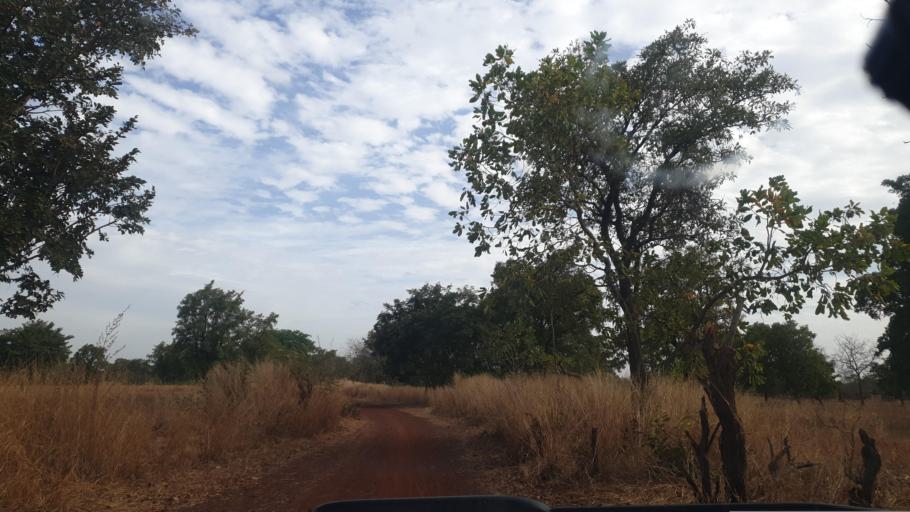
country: ML
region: Sikasso
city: Yanfolila
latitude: 11.3901
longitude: -8.0229
